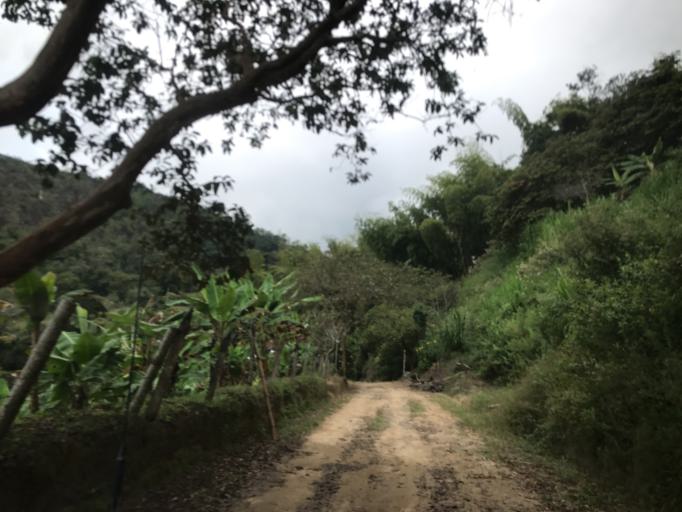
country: CO
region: Valle del Cauca
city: Obando
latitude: 4.5639
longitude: -75.8970
